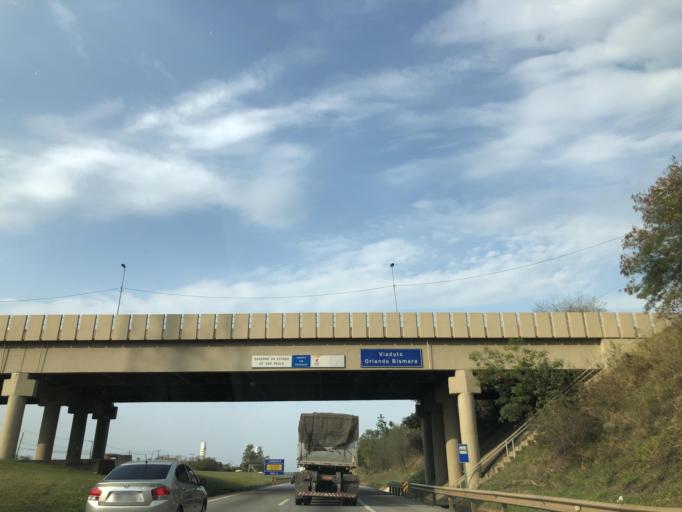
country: BR
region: Sao Paulo
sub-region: Sorocaba
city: Sorocaba
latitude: -23.4402
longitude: -47.3797
